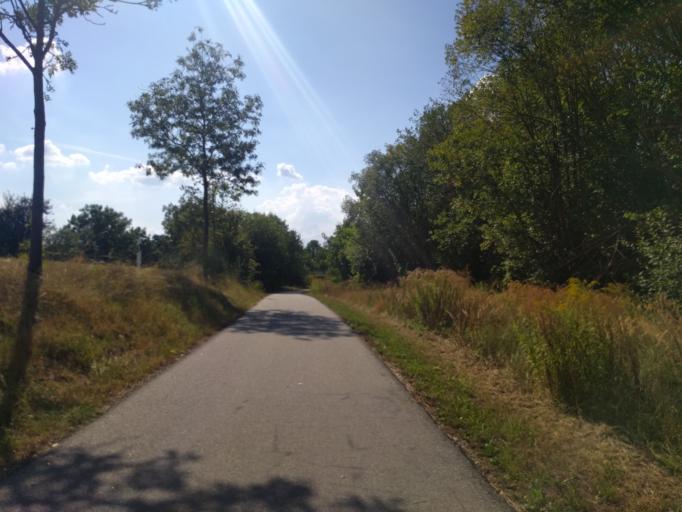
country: DE
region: Bavaria
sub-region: Upper Palatinate
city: Barbing
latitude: 49.0053
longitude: 12.2112
